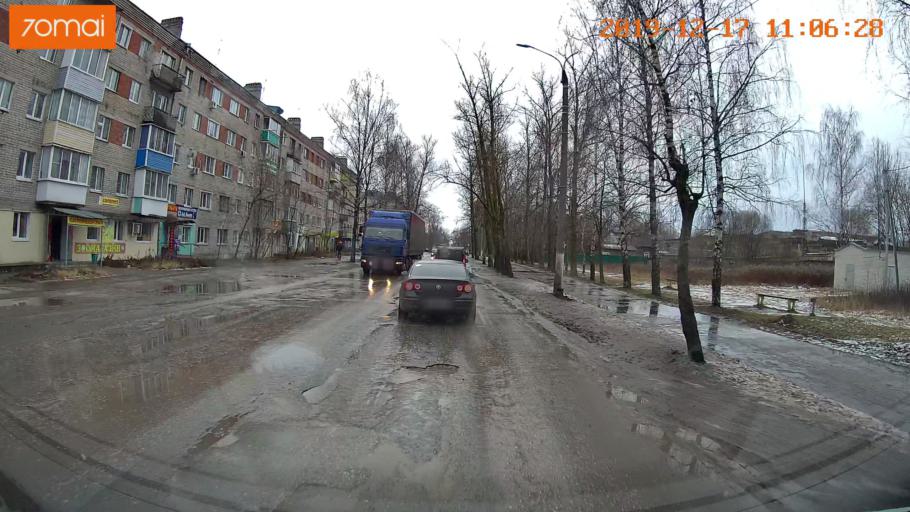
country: RU
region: Vladimir
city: Gus'-Khrustal'nyy
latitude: 55.6155
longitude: 40.6446
